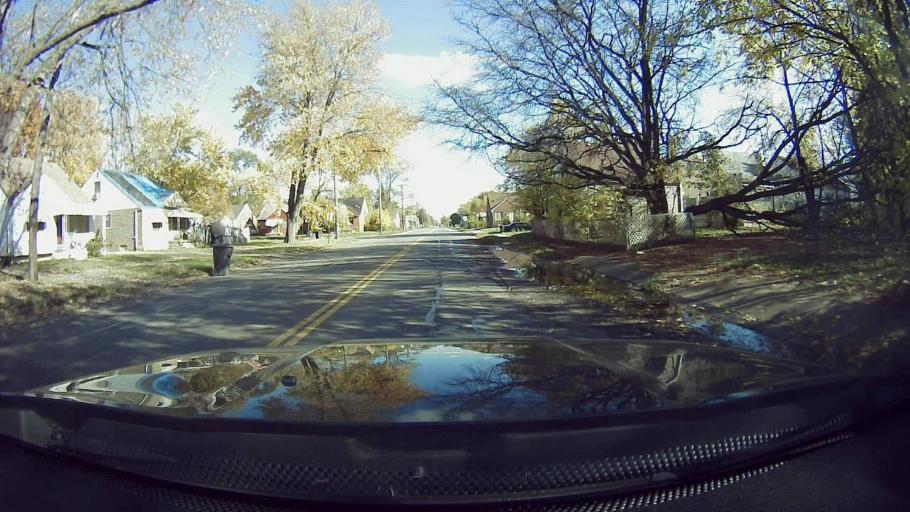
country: US
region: Michigan
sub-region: Wayne County
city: Dearborn Heights
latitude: 42.3505
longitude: -83.2232
